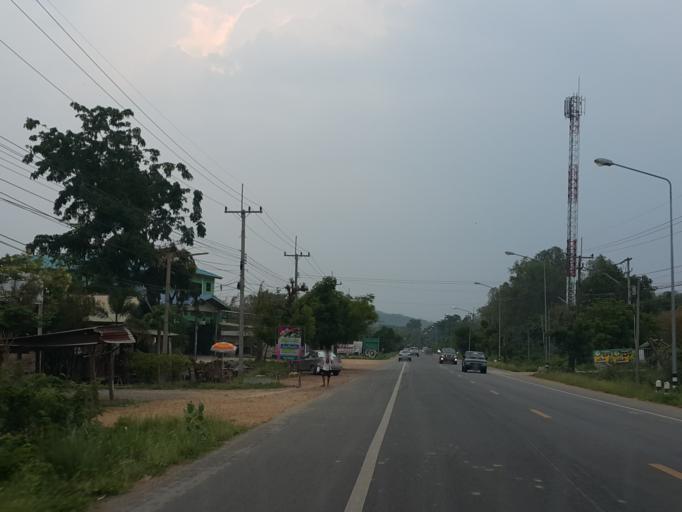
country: TH
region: Uthai Thani
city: Ban Rai
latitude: 15.0875
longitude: 99.5813
